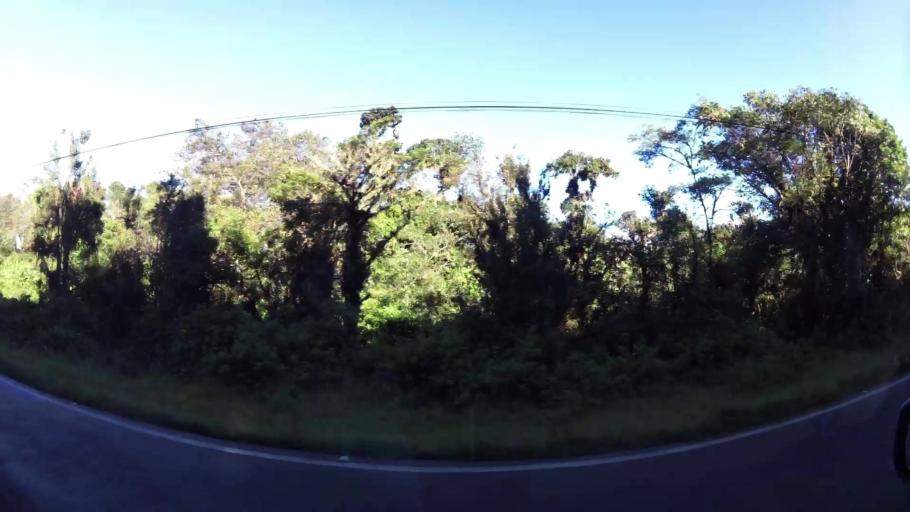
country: CR
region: San Jose
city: San Marcos
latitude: 9.7002
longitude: -83.9402
